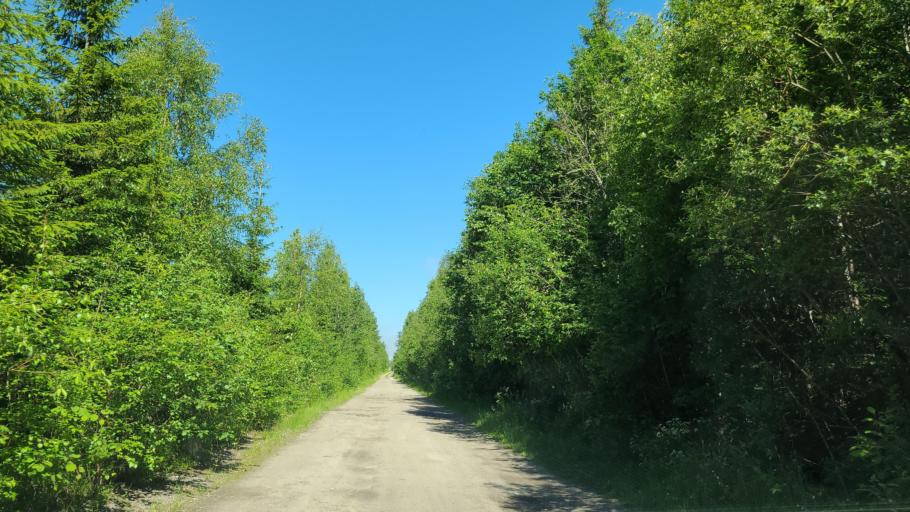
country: SE
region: Vaesternorrland
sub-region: OErnskoeldsviks Kommun
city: Husum
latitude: 63.4225
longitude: 19.2242
